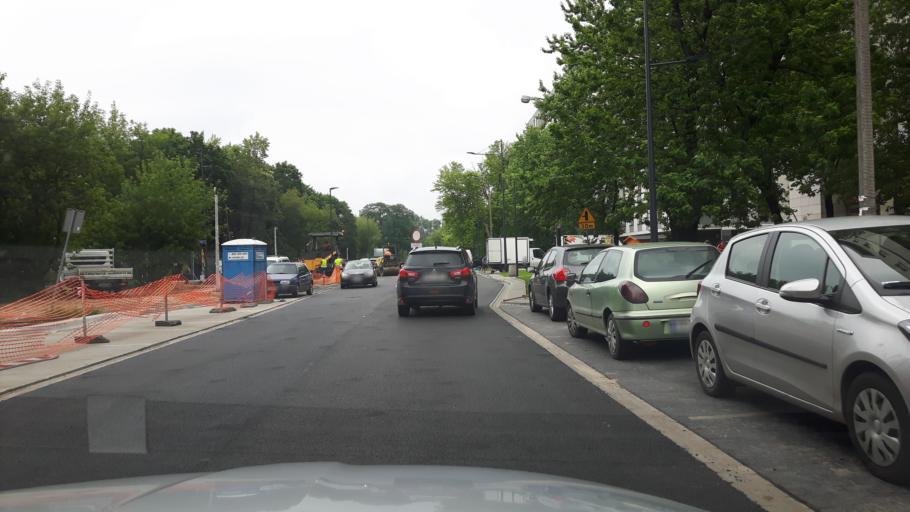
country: PL
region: Masovian Voivodeship
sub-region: Warszawa
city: Zoliborz
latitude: 52.2593
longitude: 20.9736
